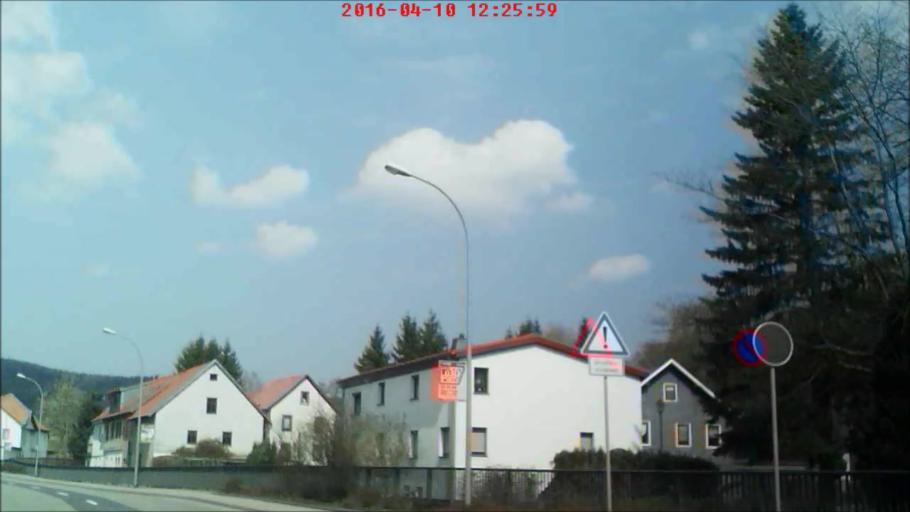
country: DE
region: Thuringia
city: Steinbach-Hallenberg
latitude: 50.6821
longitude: 10.5571
